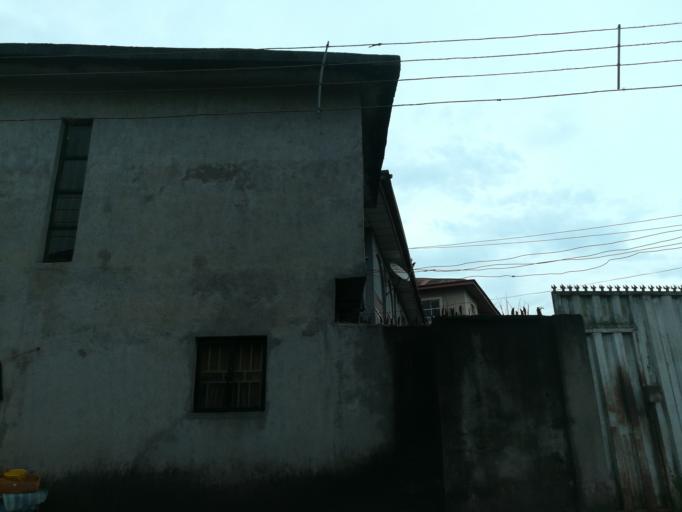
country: NG
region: Rivers
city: Port Harcourt
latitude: 4.8587
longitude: 7.0335
